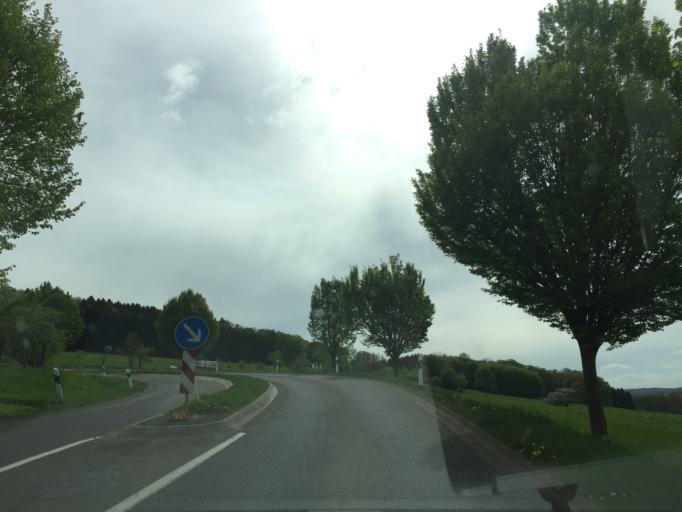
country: DE
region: Rheinland-Pfalz
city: Hahn bei Marienberg
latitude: 50.6310
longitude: 7.9396
